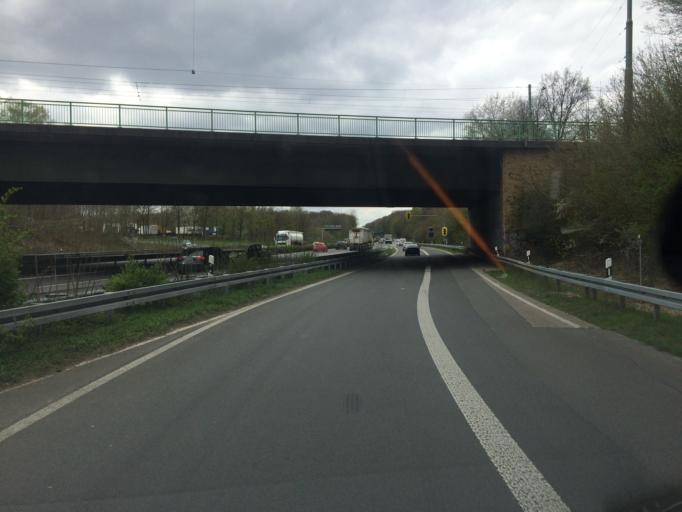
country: DE
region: North Rhine-Westphalia
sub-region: Regierungsbezirk Arnsberg
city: Bochum
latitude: 51.5031
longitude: 7.2601
